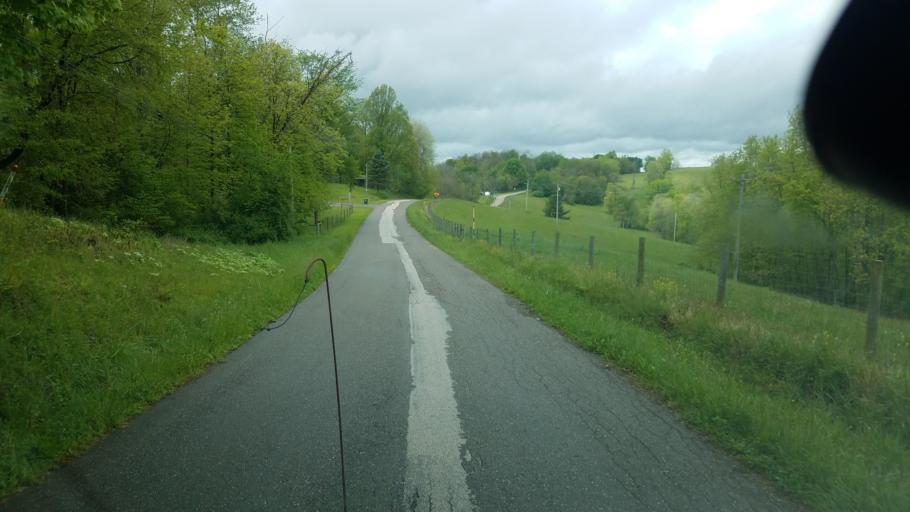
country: US
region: Ohio
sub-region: Tuscarawas County
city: Rockford
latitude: 40.4055
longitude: -81.1992
